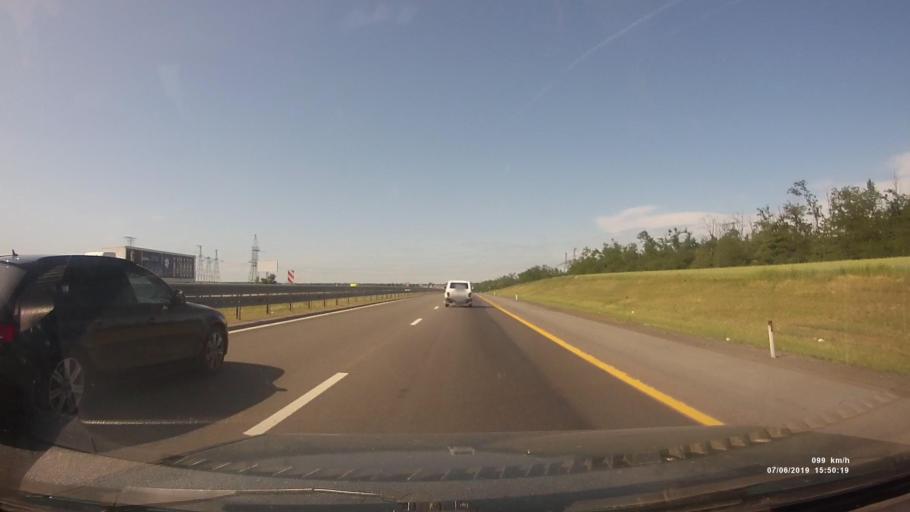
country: RU
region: Rostov
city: Ayutinskiy
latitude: 47.8035
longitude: 40.1704
